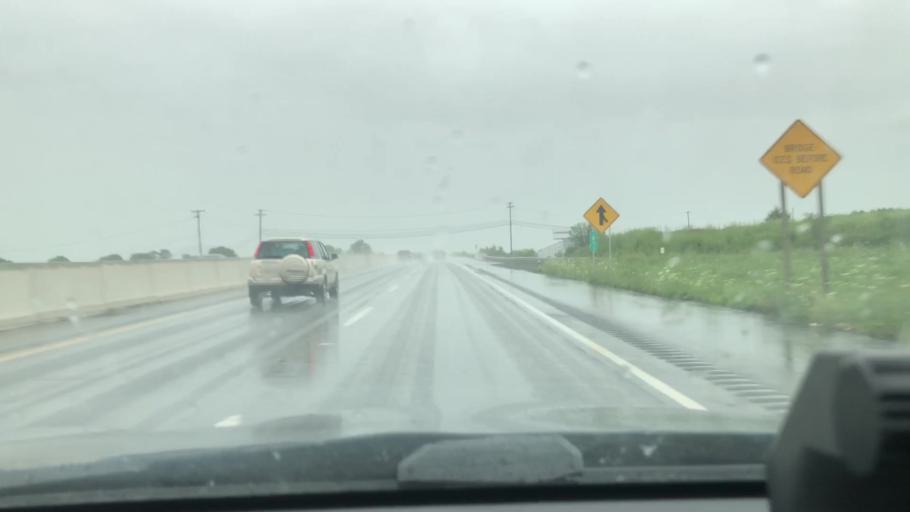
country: US
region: Pennsylvania
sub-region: Northampton County
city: Wind Gap
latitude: 40.8347
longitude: -75.2996
